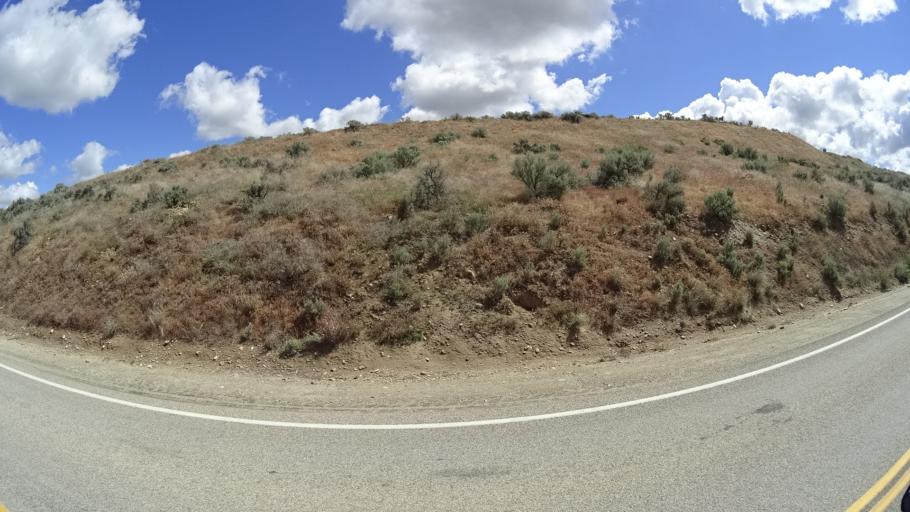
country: US
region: Idaho
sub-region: Ada County
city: Kuna
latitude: 43.5122
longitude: -116.3138
